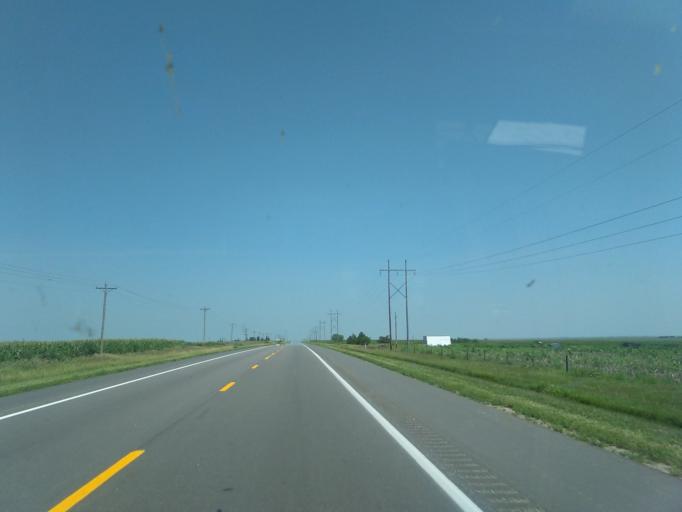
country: US
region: Nebraska
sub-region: Red Willow County
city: McCook
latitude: 40.2726
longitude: -100.6500
